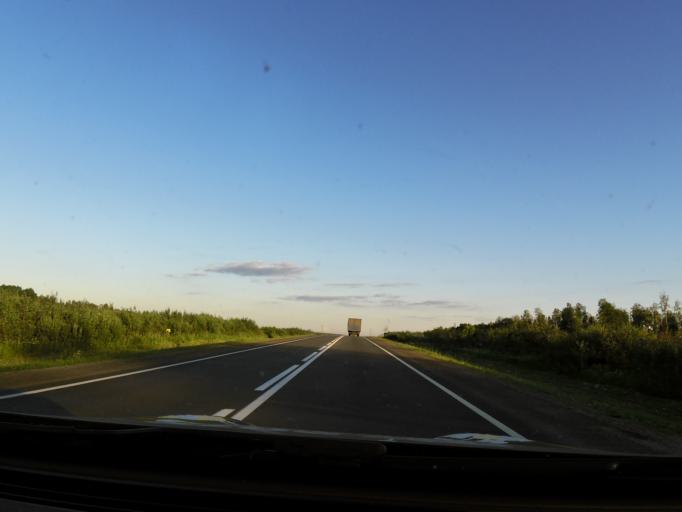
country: RU
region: Jaroslavl
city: Prechistoye
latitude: 58.6511
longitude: 40.3193
